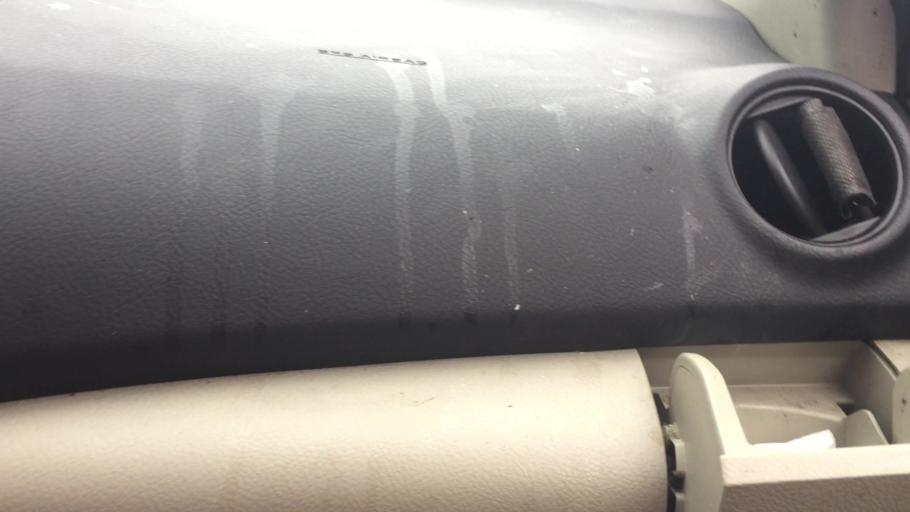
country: US
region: Illinois
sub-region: Williamson County
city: Marion
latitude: 37.7235
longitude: -88.9461
